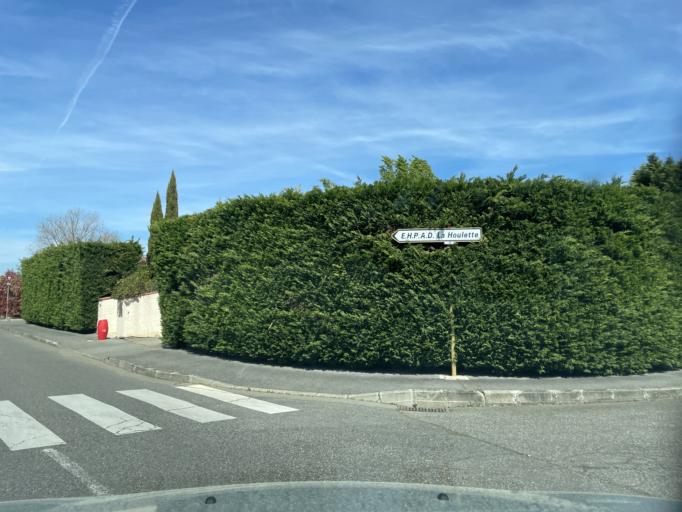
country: FR
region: Midi-Pyrenees
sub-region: Departement de la Haute-Garonne
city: Pibrac
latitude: 43.6149
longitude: 1.2697
